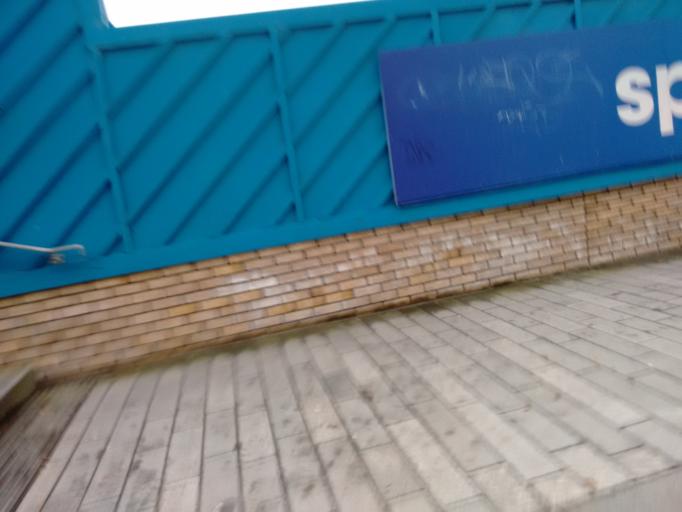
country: GB
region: Scotland
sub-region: Edinburgh
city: Edinburgh
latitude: 55.9435
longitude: -3.2141
